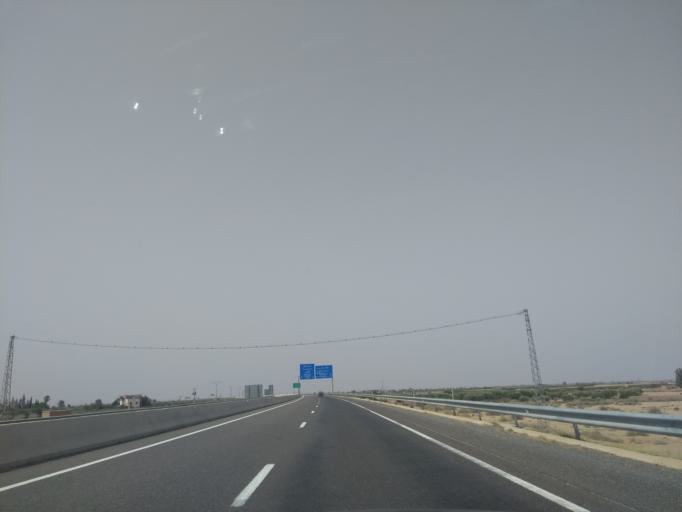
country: MA
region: Marrakech-Tensift-Al Haouz
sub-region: Chichaoua
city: Chichaoua
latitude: 31.6099
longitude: -8.3879
